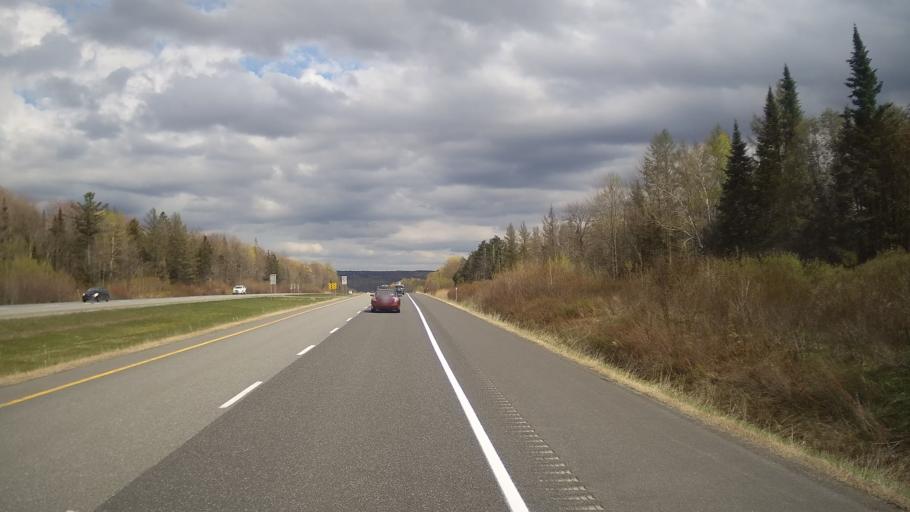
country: CA
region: Quebec
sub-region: Monteregie
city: Waterloo
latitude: 45.3036
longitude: -72.4716
